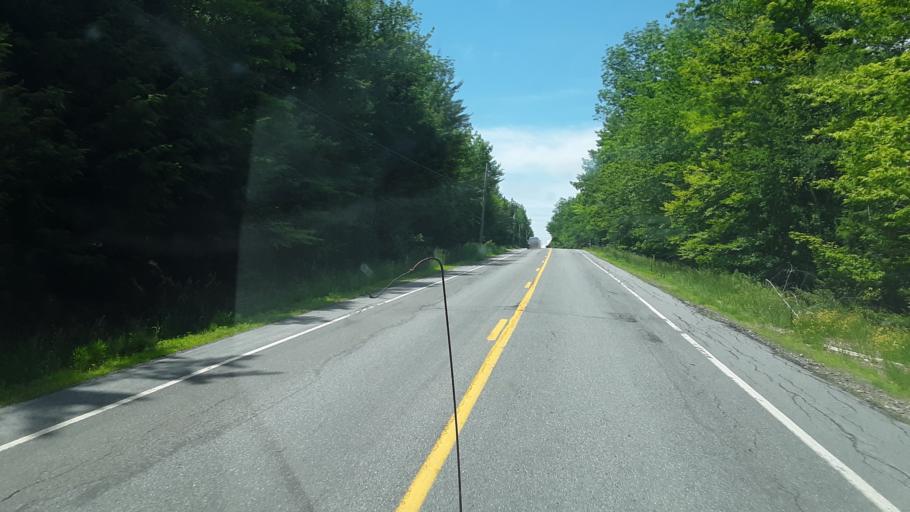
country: US
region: Maine
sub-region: Hancock County
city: Bucksport
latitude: 44.5685
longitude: -68.8285
